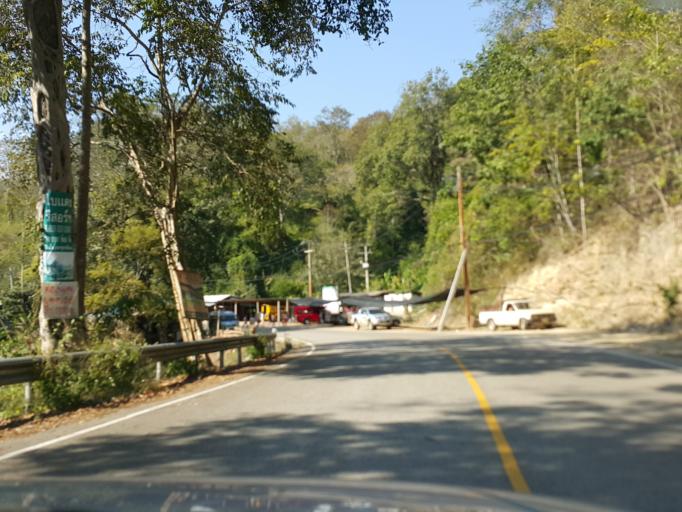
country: TH
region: Chiang Mai
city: Mae Wang
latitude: 18.6373
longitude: 98.7040
